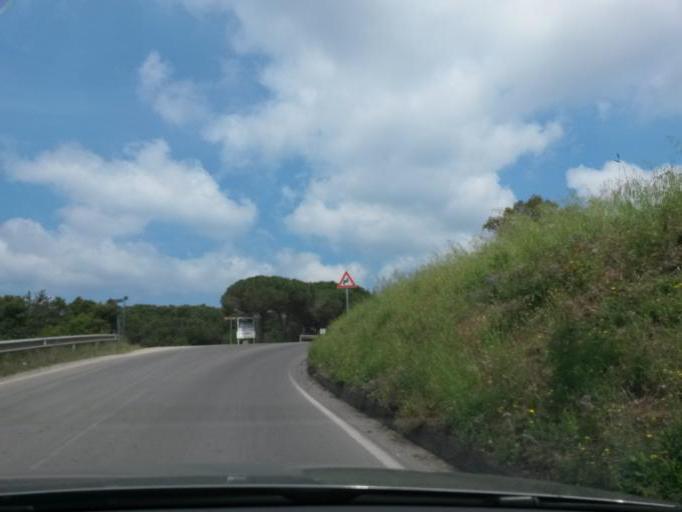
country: IT
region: Tuscany
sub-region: Provincia di Livorno
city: Portoferraio
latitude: 42.7993
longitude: 10.3314
